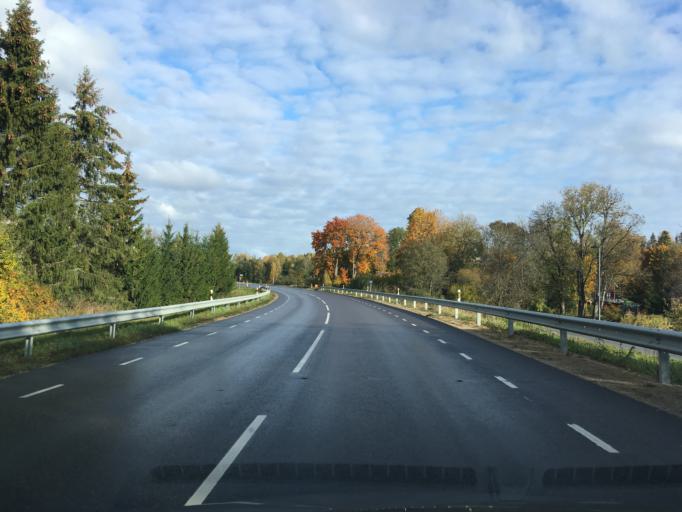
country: EE
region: Harju
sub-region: Raasiku vald
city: Raasiku
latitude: 59.1929
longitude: 25.1852
